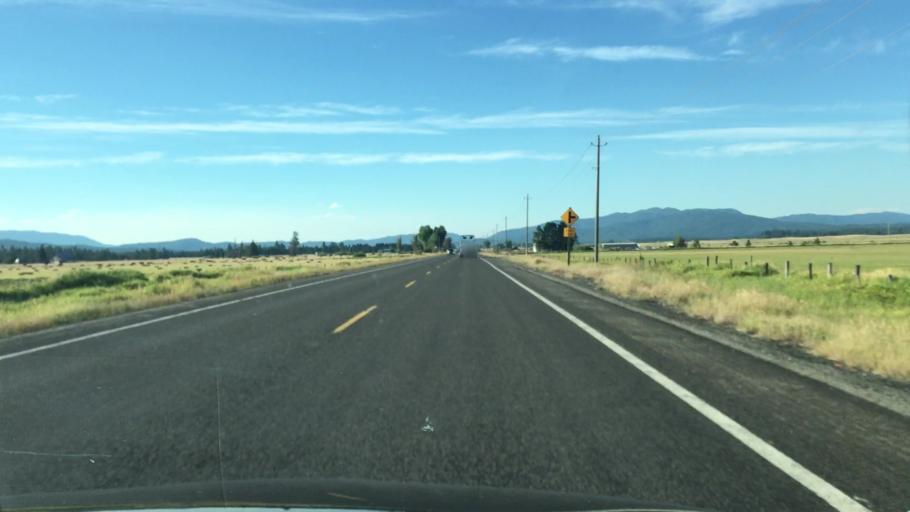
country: US
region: Idaho
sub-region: Valley County
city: Cascade
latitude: 44.4213
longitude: -115.9996
